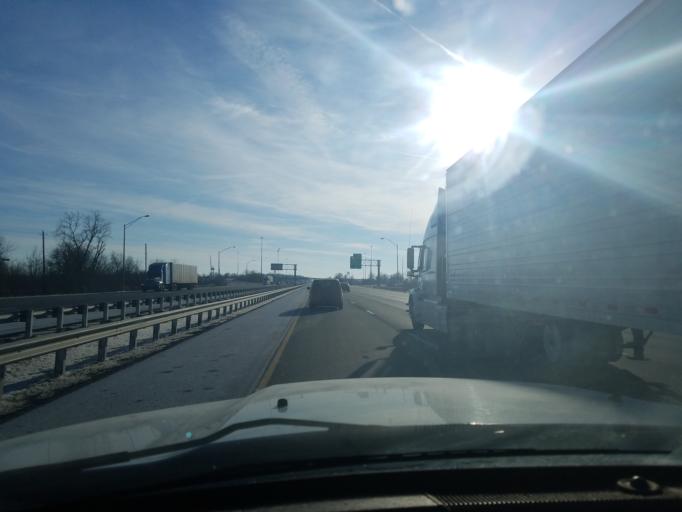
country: US
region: Indiana
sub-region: Madison County
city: Pendleton
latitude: 40.0101
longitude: -85.7695
